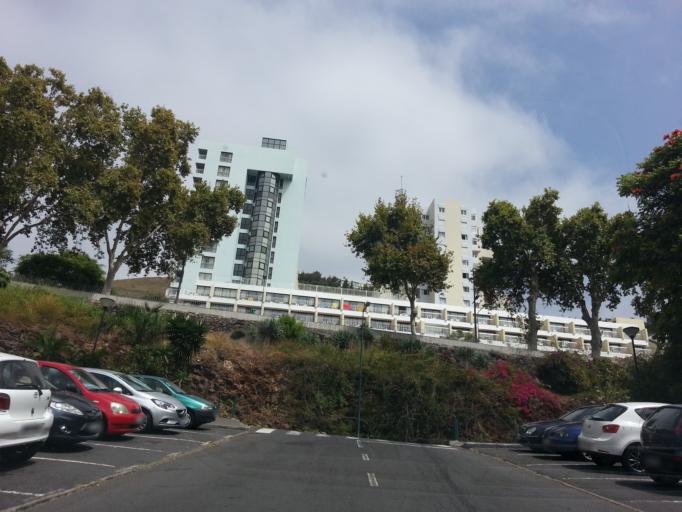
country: PT
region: Madeira
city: Camara de Lobos
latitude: 32.6375
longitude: -16.9363
